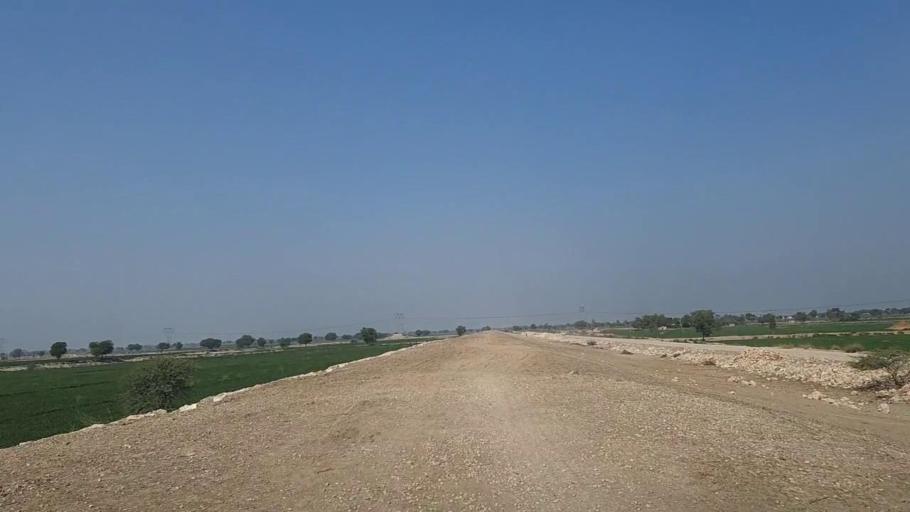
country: PK
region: Sindh
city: Moro
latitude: 26.7038
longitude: 67.9261
